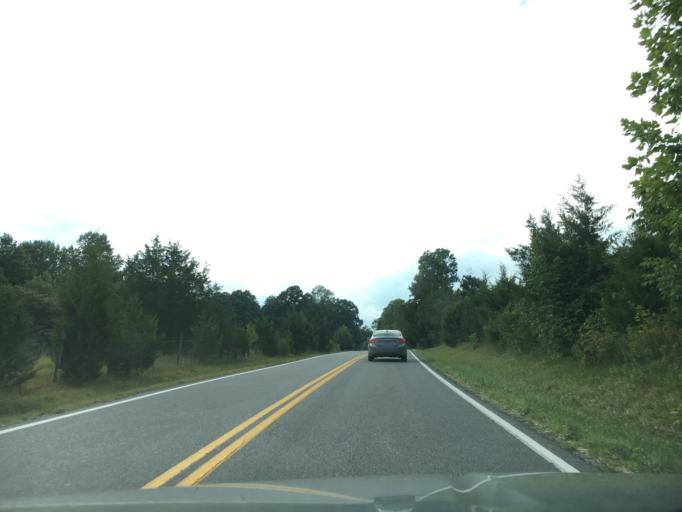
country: US
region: Virginia
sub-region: Campbell County
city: Rustburg
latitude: 37.2539
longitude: -79.1374
